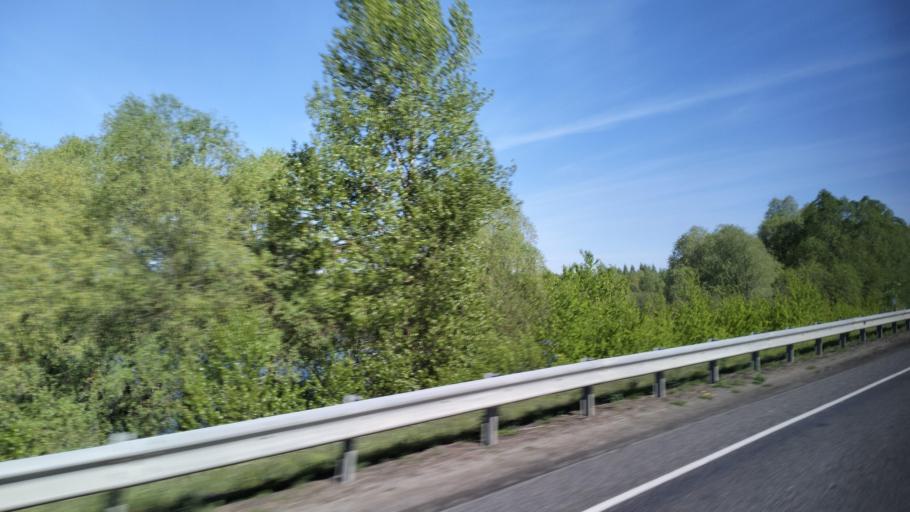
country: BY
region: Gomel
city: Turaw
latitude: 52.0910
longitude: 27.8287
